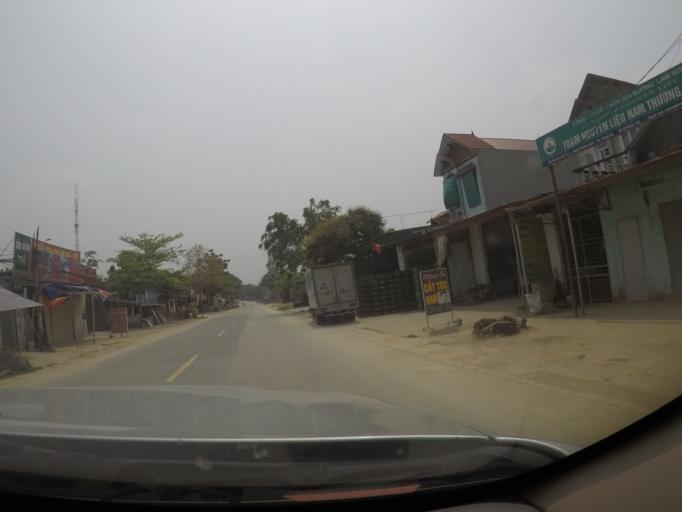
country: VN
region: Thanh Hoa
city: Thi Tran Thuong Xuan
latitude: 19.8071
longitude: 105.3954
